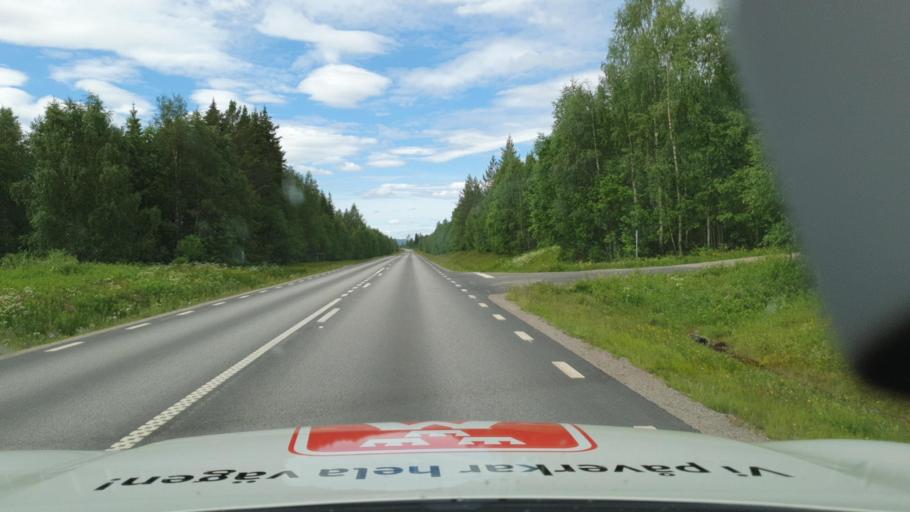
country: SE
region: Vaesterbotten
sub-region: Norsjo Kommun
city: Norsjoe
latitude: 65.2072
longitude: 19.7978
